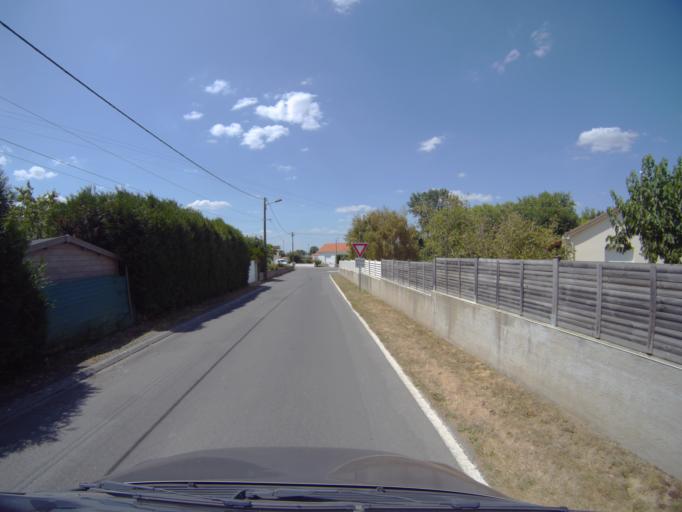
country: FR
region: Pays de la Loire
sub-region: Departement de la Loire-Atlantique
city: La Planche
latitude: 47.0171
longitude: -1.4320
